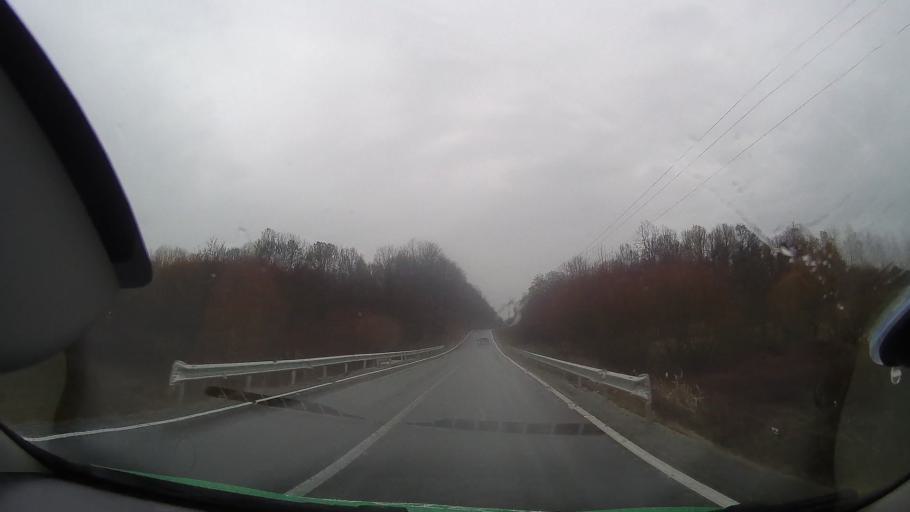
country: RO
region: Bihor
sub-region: Comuna Olcea
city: Olcea
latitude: 46.6935
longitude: 21.9652
